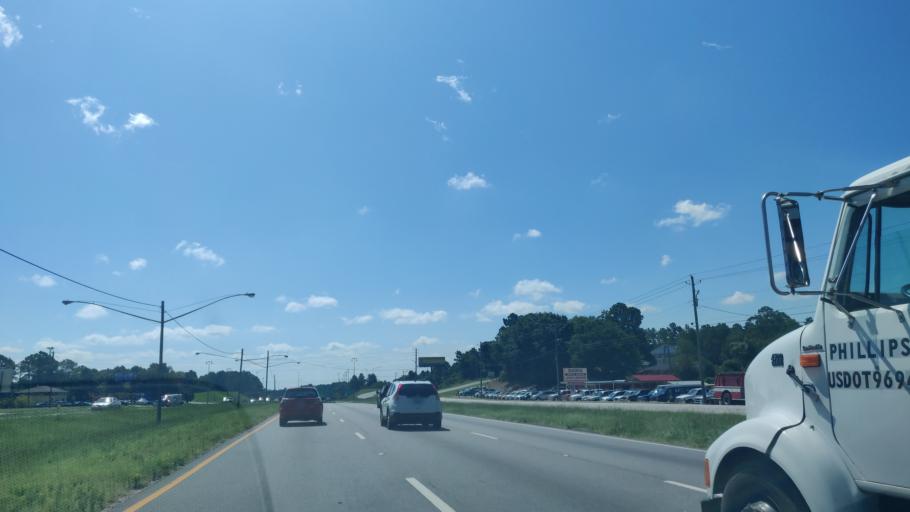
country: US
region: Alabama
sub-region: Russell County
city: Phenix City
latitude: 32.4592
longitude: -85.0166
